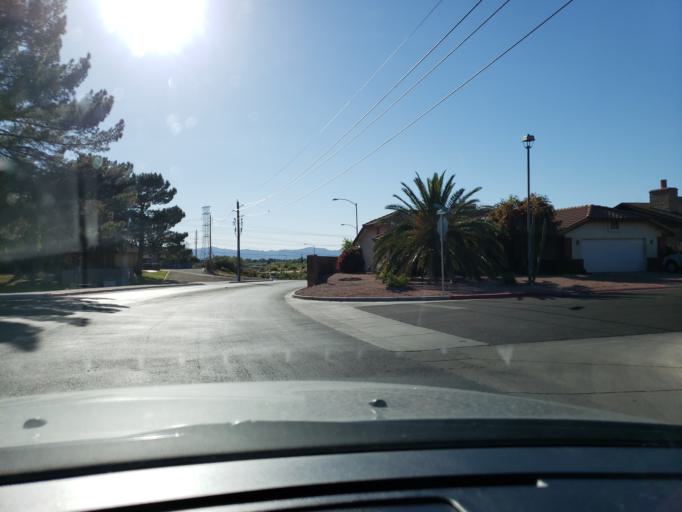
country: US
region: Arizona
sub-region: Maricopa County
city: Youngtown
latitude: 33.5801
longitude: -112.3044
